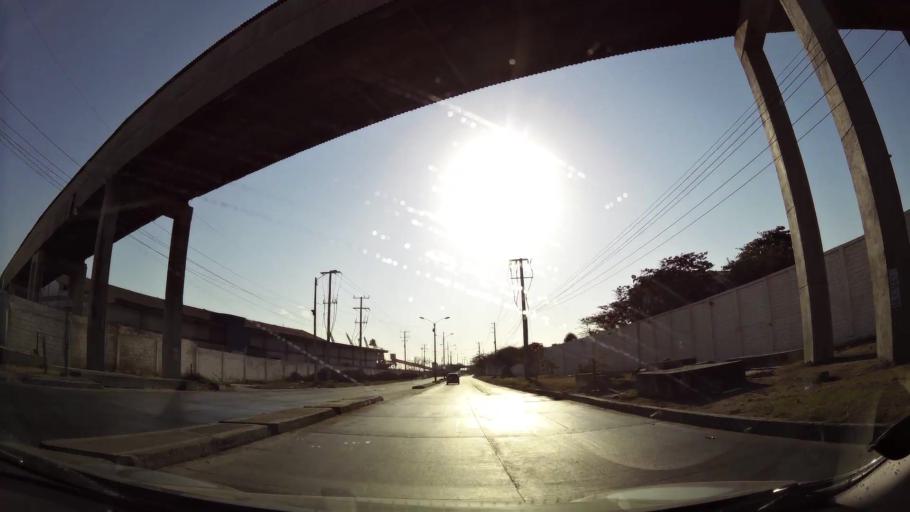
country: CO
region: Atlantico
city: Barranquilla
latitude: 11.0380
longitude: -74.8193
